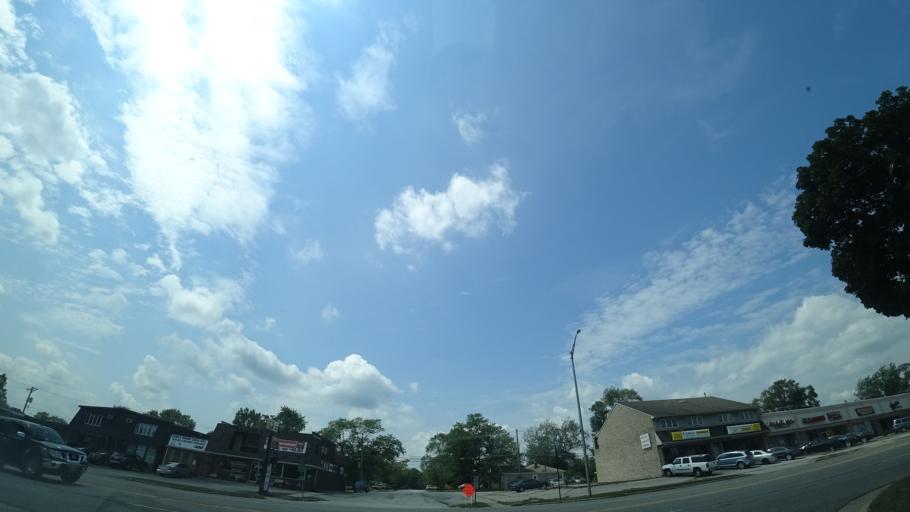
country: US
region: Illinois
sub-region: Cook County
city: Worth
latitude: 41.6852
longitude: -87.7971
